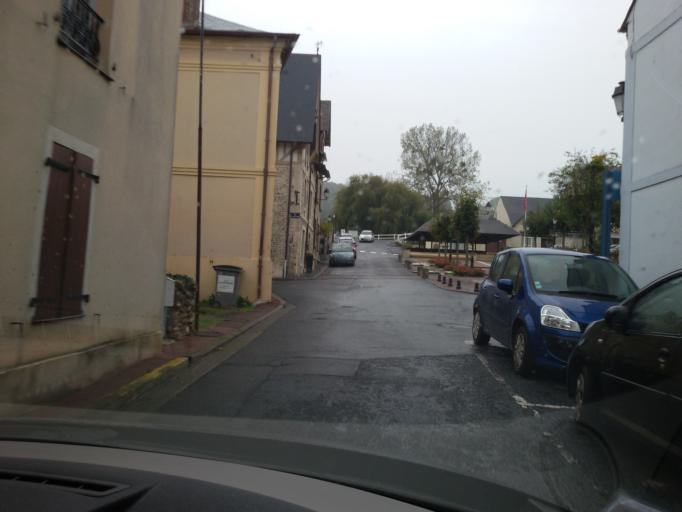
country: FR
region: Lower Normandy
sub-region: Departement du Calvados
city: Trouville-sur-Mer
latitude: 49.4000
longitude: 0.1269
